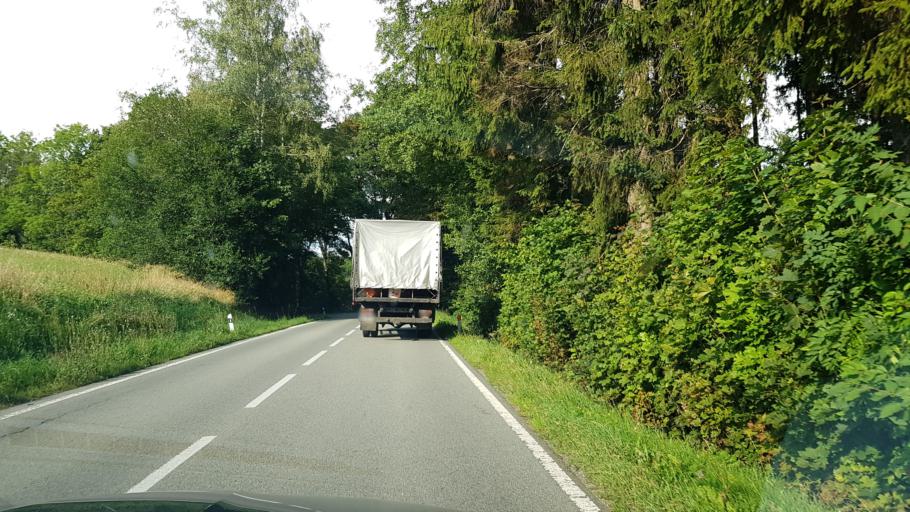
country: CZ
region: Pardubicky
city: Jablonne nad Orlici
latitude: 50.0906
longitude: 16.6058
